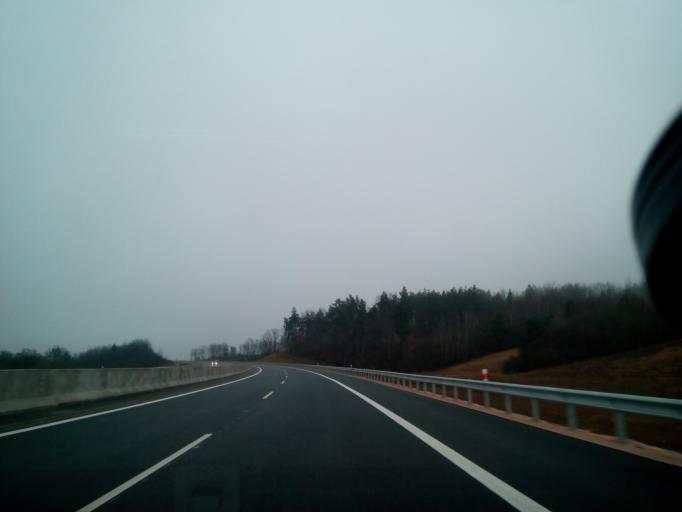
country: SK
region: Presovsky
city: Sabinov
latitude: 49.0122
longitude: 21.0427
